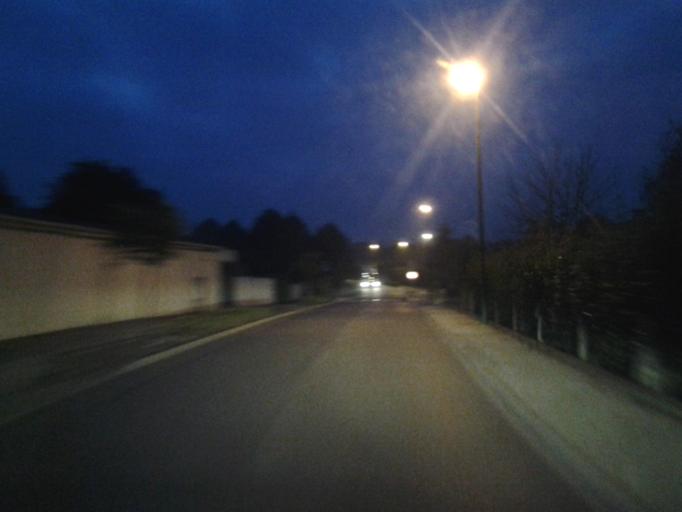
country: FR
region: Pays de la Loire
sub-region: Departement de la Vendee
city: Landeronde
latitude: 46.6559
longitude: -1.5653
